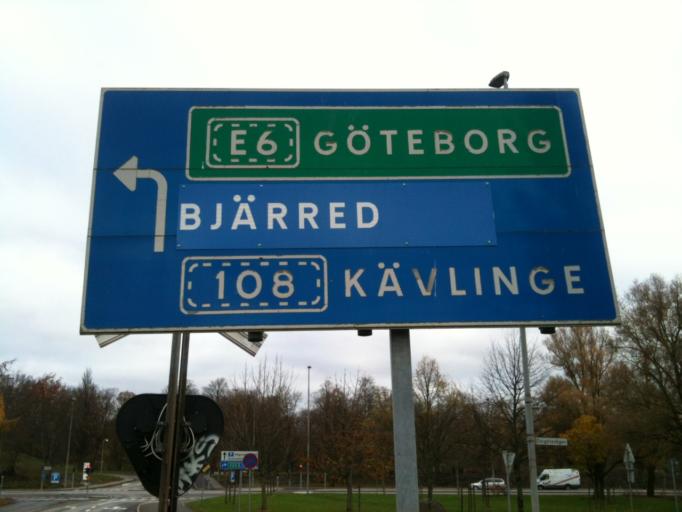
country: SE
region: Skane
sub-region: Lunds Kommun
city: Lund
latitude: 55.6958
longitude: 13.1833
